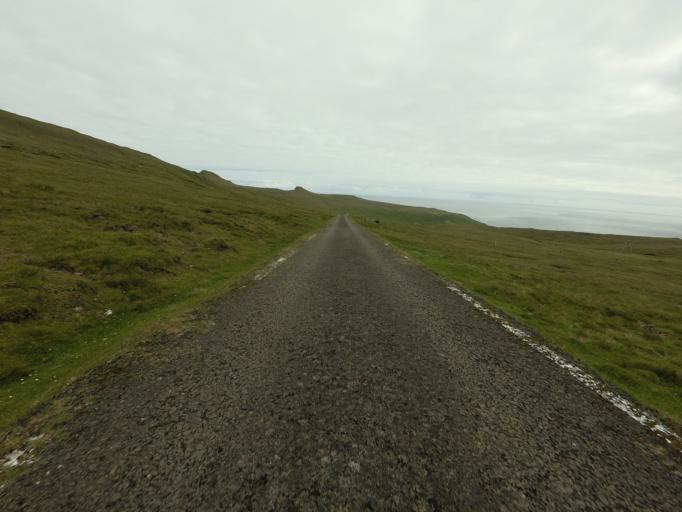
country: FO
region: Suduroy
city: Vagur
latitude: 61.4174
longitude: -6.7309
